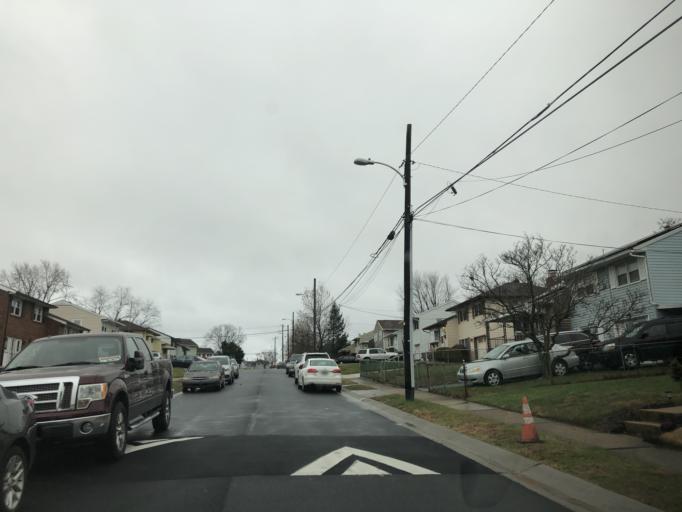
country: US
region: Delaware
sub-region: New Castle County
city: Wilmington Manor
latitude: 39.7105
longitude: -75.5603
